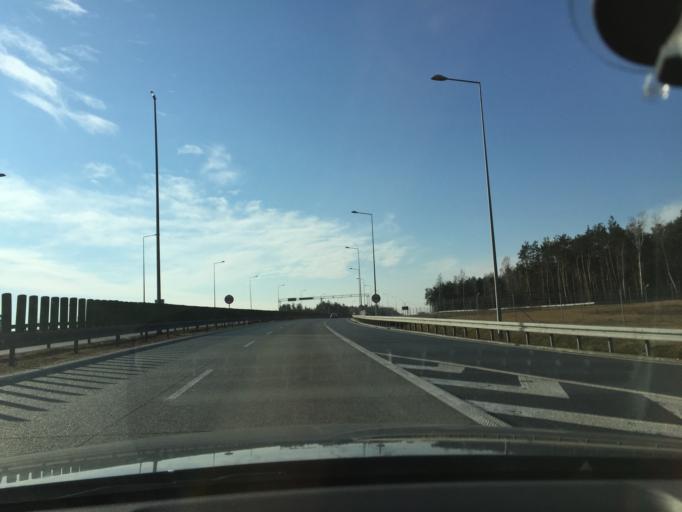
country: PL
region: Lodz Voivodeship
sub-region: Powiat rawski
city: Rawa Mazowiecka
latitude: 51.7047
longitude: 20.2201
